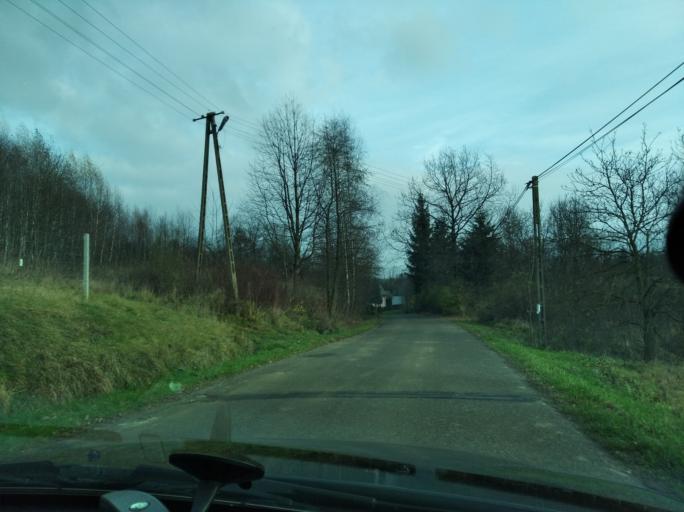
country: PL
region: Subcarpathian Voivodeship
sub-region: Powiat przeworski
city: Sietesz
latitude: 49.9664
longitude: 22.3520
